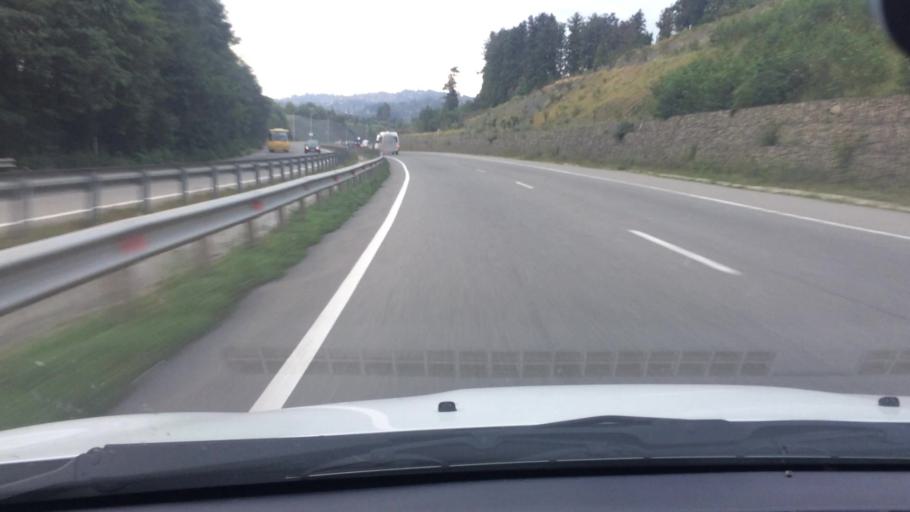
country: GE
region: Ajaria
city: Makhinjauri
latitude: 41.6957
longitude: 41.7269
